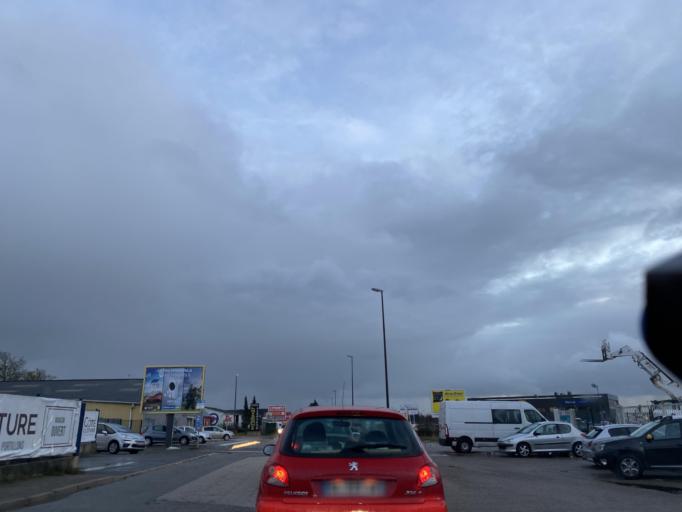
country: FR
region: Haute-Normandie
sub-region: Departement de l'Eure
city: Evreux
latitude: 49.0176
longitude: 1.1853
